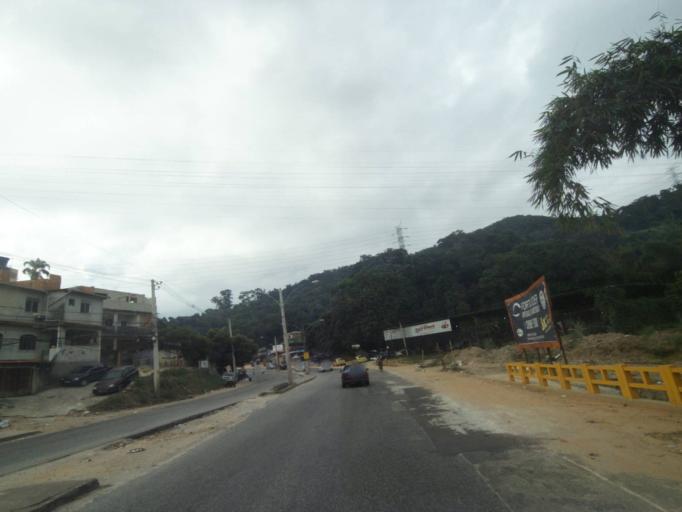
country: BR
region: Rio de Janeiro
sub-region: Sao Joao De Meriti
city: Sao Joao de Meriti
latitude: -22.9067
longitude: -43.3797
